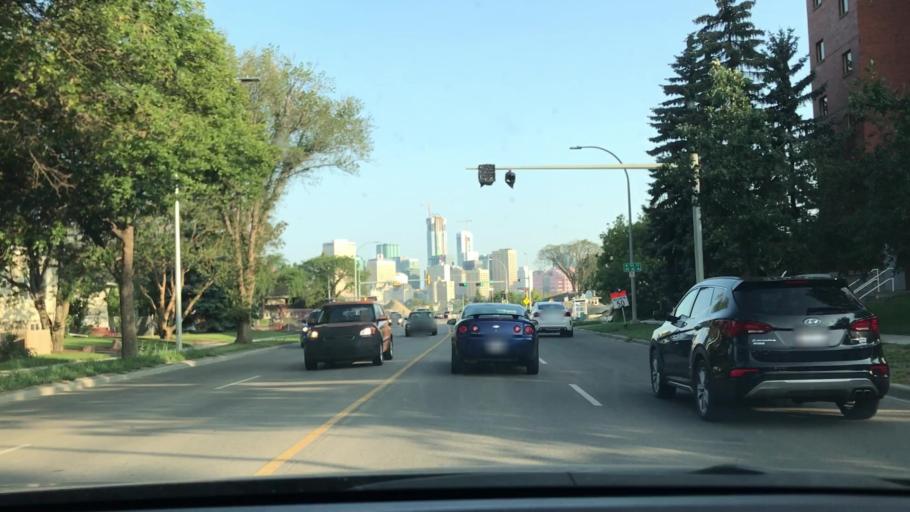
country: CA
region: Alberta
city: Edmonton
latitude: 53.5308
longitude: -113.4697
